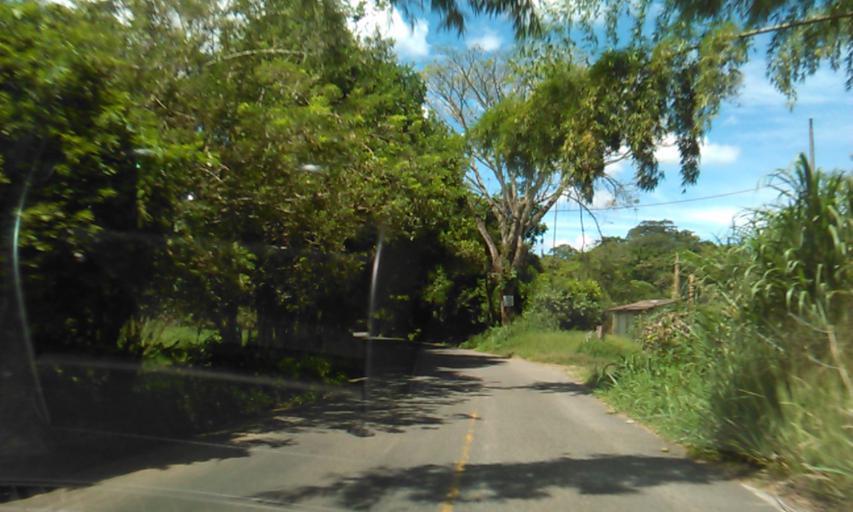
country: CO
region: Quindio
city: Cordoba
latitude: 4.4018
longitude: -75.7220
